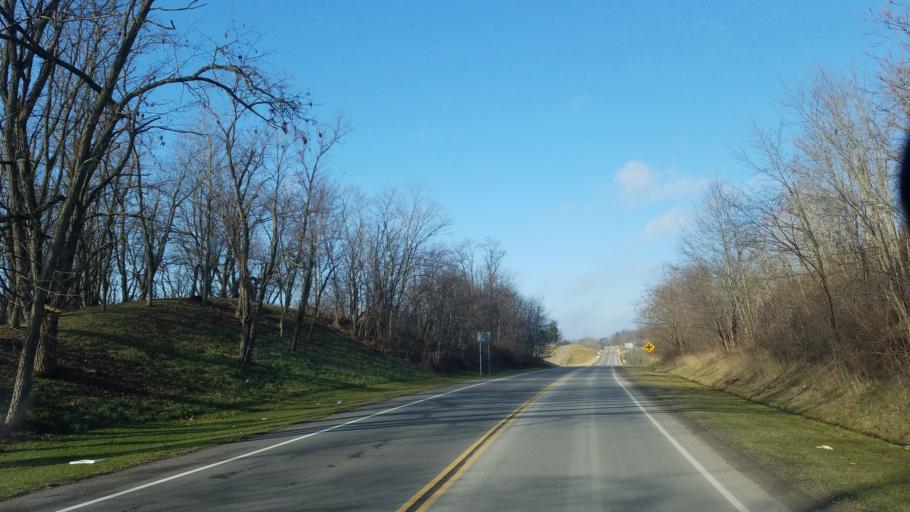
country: US
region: Ohio
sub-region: Guernsey County
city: Byesville
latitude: 40.0363
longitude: -81.4362
